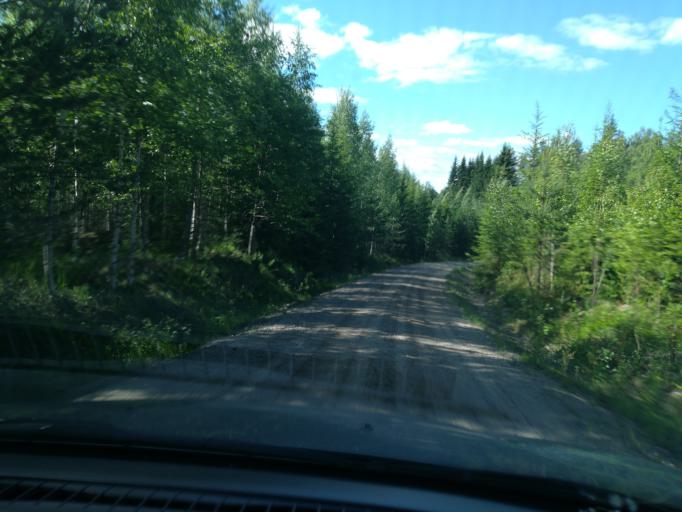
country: FI
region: Southern Savonia
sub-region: Mikkeli
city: Puumala
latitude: 61.6559
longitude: 28.1637
